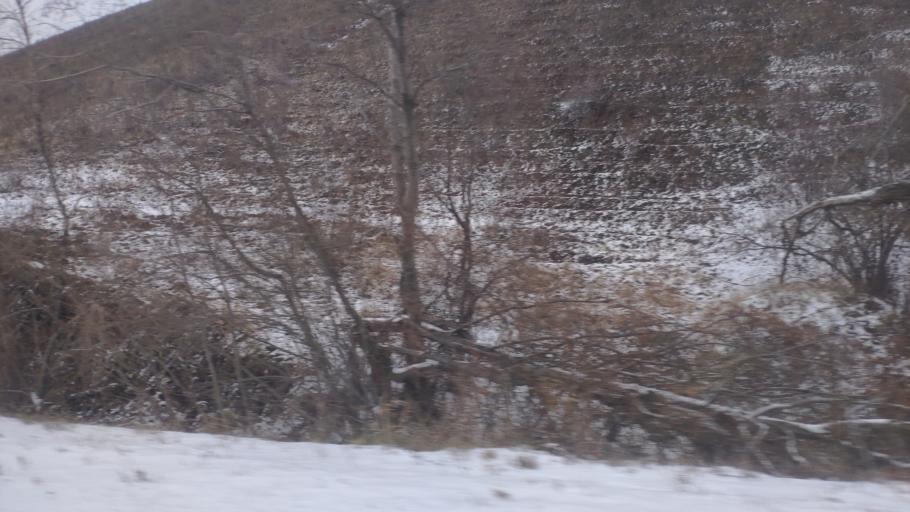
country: RU
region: Bashkortostan
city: Isyangulovo
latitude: 52.1614
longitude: 56.9161
